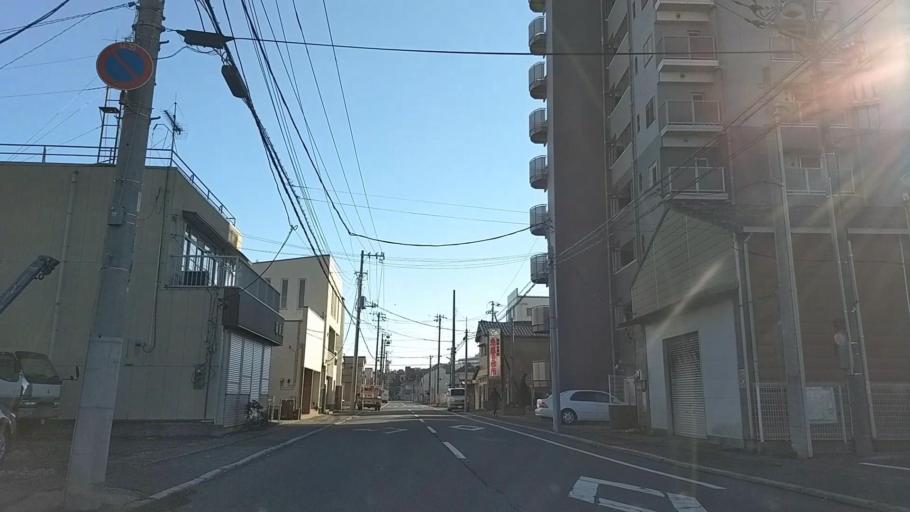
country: JP
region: Chiba
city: Hasaki
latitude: 35.7336
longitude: 140.8371
